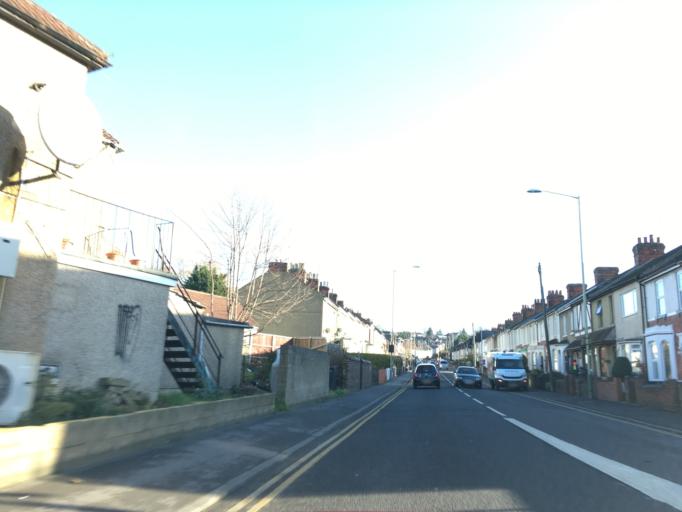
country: GB
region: England
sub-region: Borough of Swindon
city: Swindon
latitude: 51.5547
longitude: -1.7963
